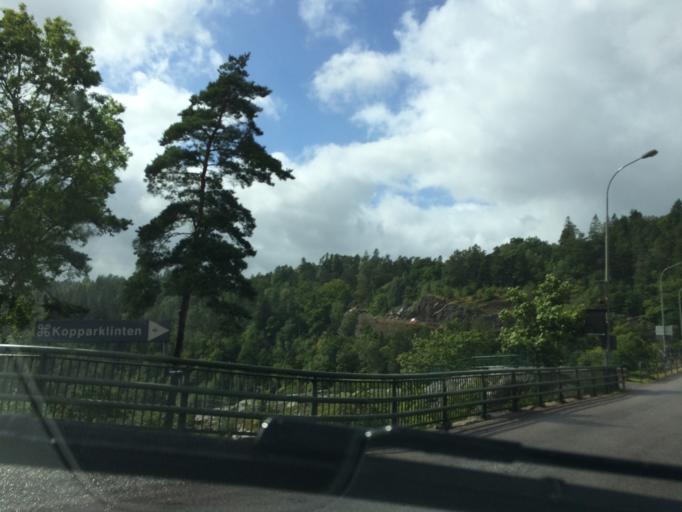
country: SE
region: Vaestra Goetaland
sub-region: Trollhattan
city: Trollhattan
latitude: 58.2798
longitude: 12.2793
